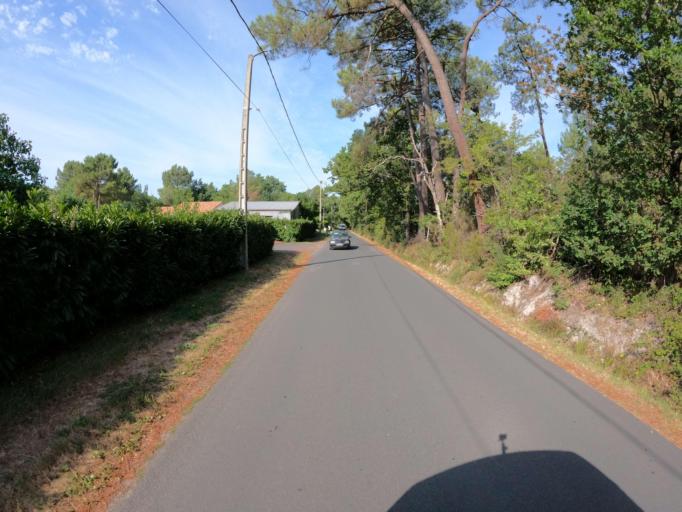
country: FR
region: Pays de la Loire
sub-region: Departement de la Vendee
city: Soullans
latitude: 46.8057
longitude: -1.8692
